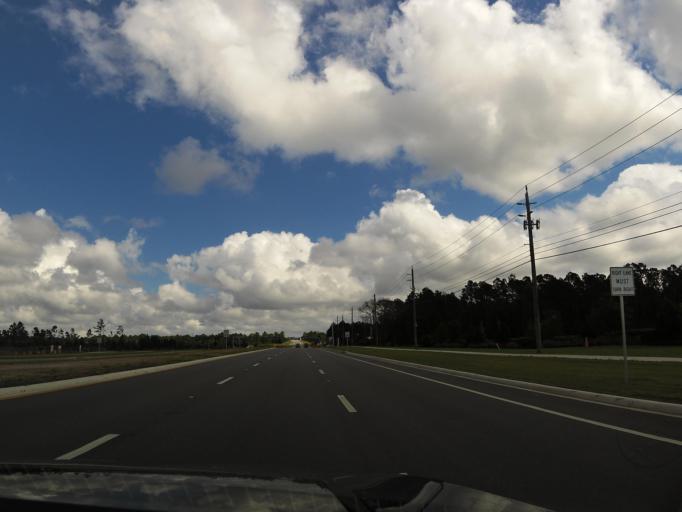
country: US
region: Florida
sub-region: Saint Johns County
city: Palm Valley
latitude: 30.0849
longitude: -81.4713
